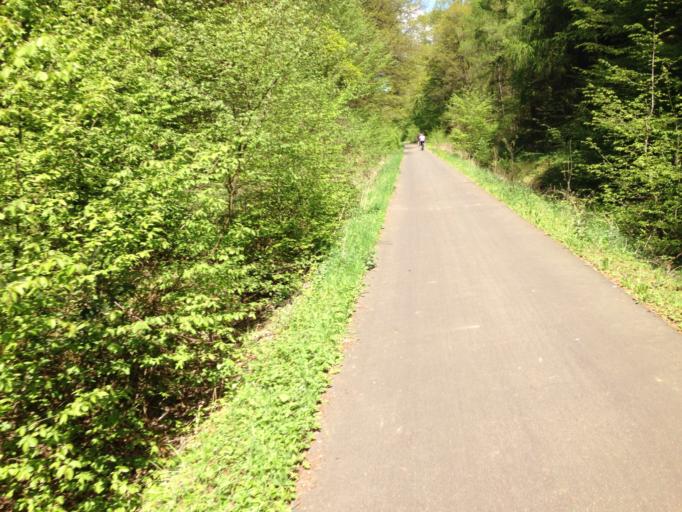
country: DE
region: Hesse
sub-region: Regierungsbezirk Giessen
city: Hungen
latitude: 50.4945
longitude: 8.9057
